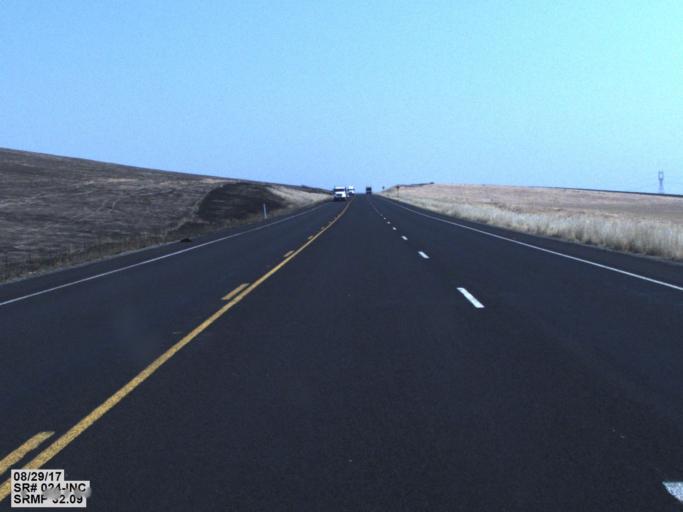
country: US
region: Washington
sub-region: Grant County
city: Desert Aire
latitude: 46.5418
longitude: -119.8483
